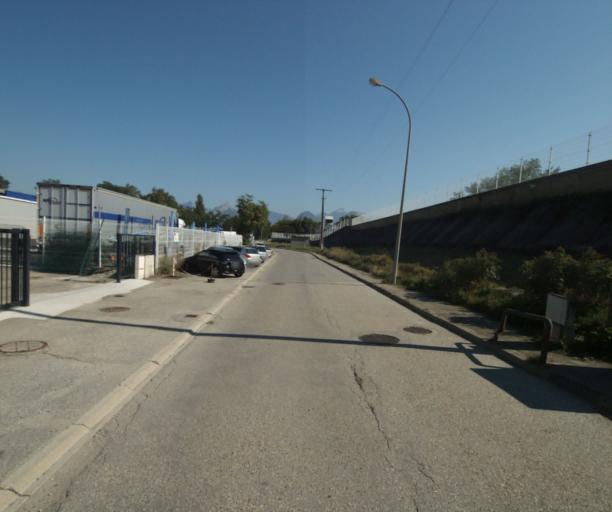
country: FR
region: Rhone-Alpes
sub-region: Departement de l'Isere
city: Le Pont-de-Claix
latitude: 45.1379
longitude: 5.6957
